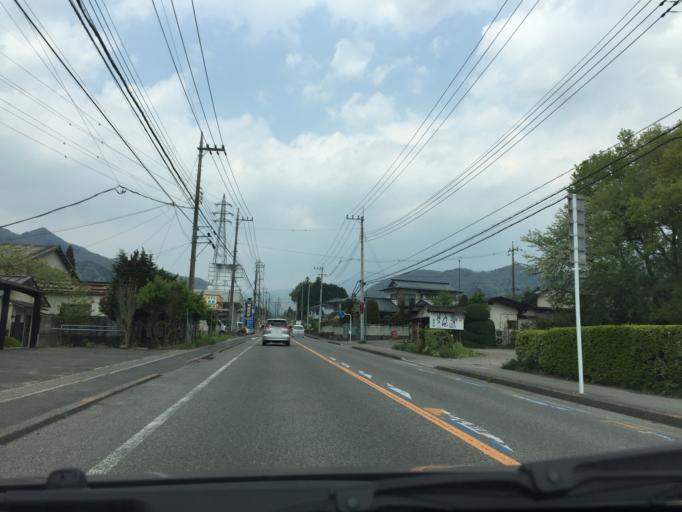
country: JP
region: Tochigi
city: Imaichi
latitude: 36.8033
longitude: 139.7072
